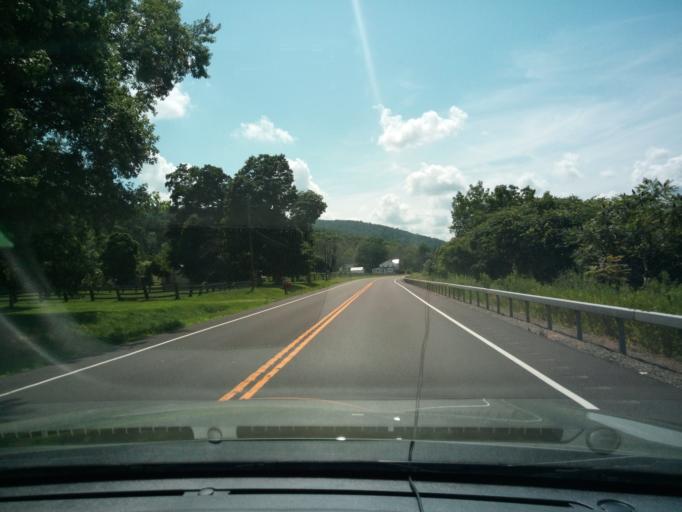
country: US
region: New York
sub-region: Chemung County
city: Southport
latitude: 42.0187
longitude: -76.6861
